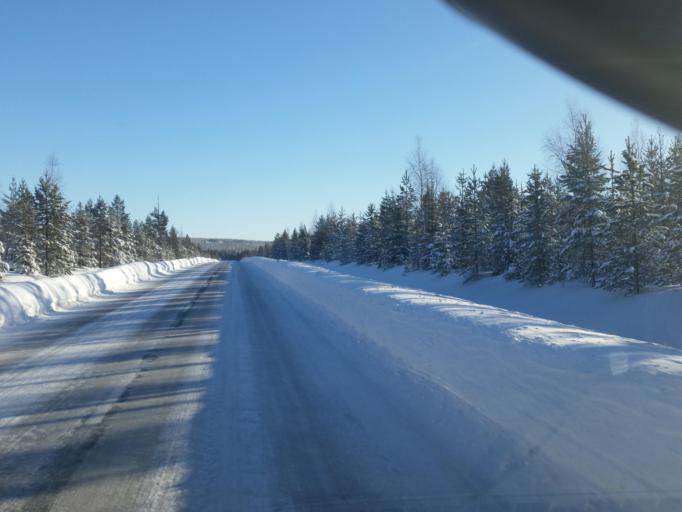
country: SE
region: Vaesterbotten
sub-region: Skelleftea Kommun
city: Storvik
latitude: 65.3273
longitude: 20.6758
